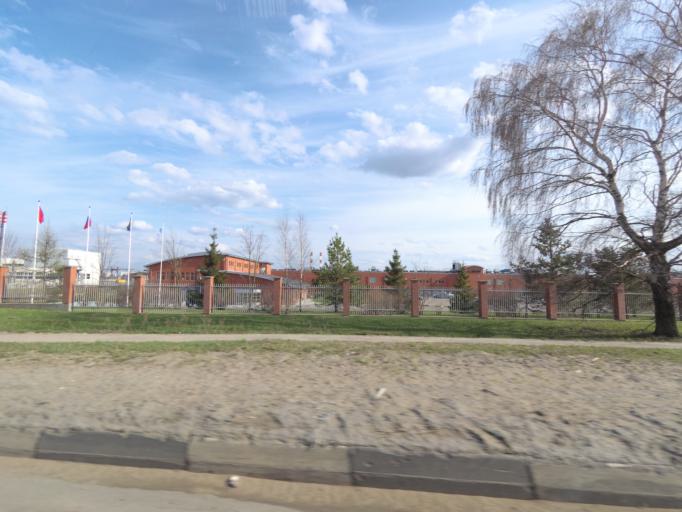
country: RU
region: Moskovskaya
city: Lobnya
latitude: 56.0258
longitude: 37.4307
